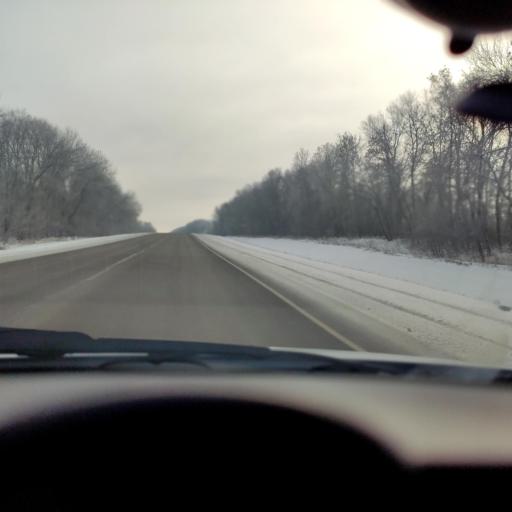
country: RU
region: Kursk
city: Kirovskiy
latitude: 51.6832
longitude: 36.5684
